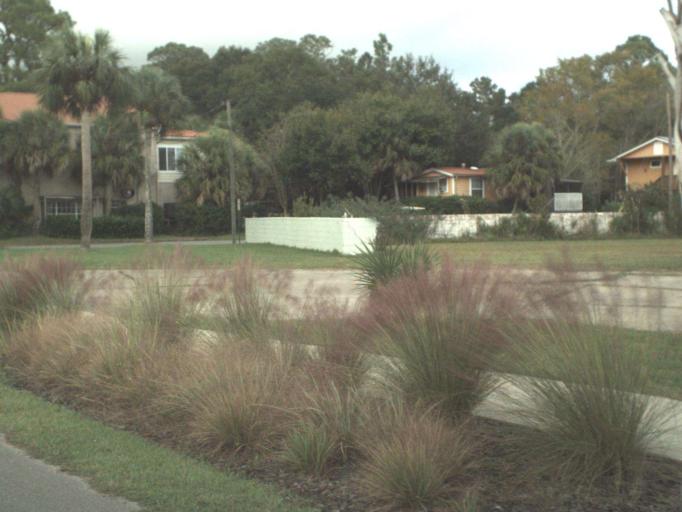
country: US
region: Florida
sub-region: Leon County
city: Woodville
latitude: 30.1564
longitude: -84.2041
